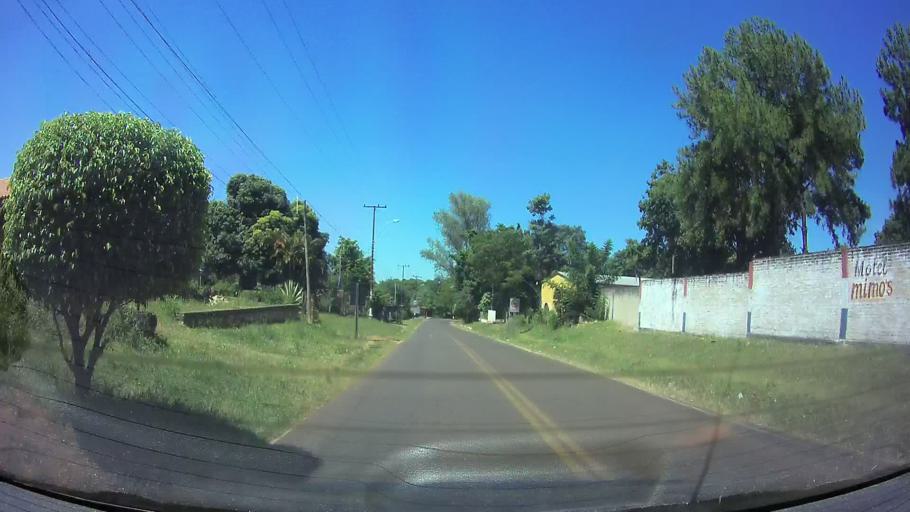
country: PY
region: Central
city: Aregua
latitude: -25.2906
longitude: -57.4101
